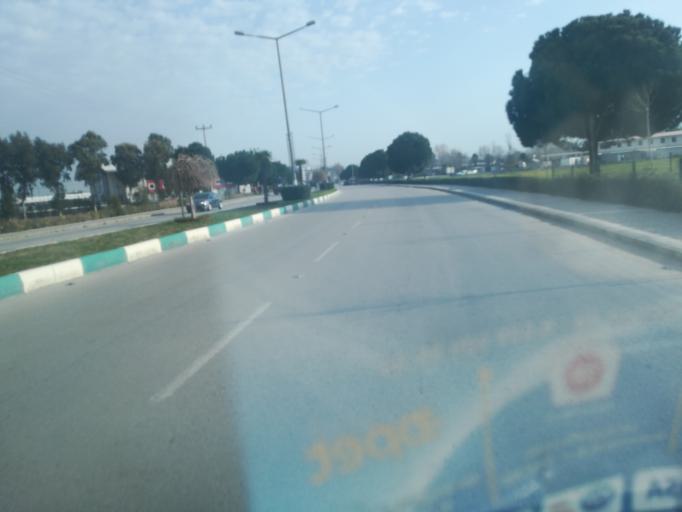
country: TR
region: Osmaniye
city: Osmaniye
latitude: 37.0511
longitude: 36.2293
